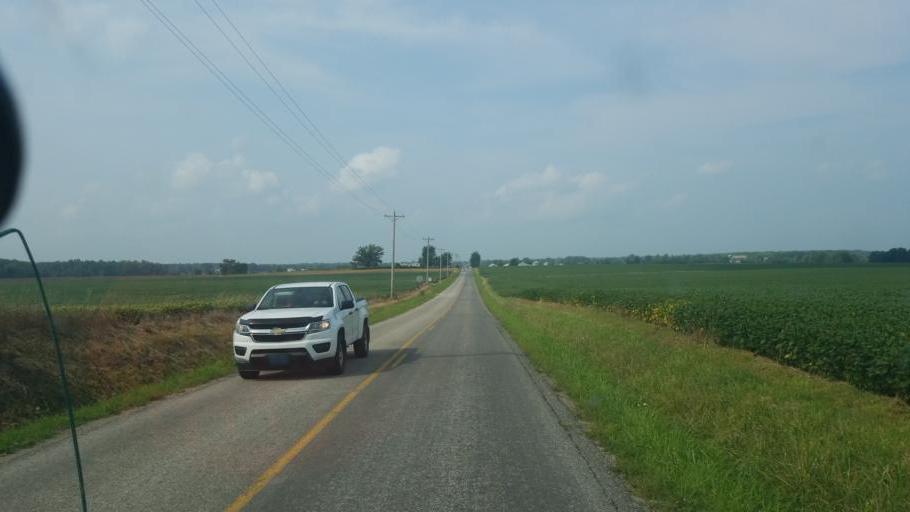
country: US
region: Ohio
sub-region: Lorain County
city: Wellington
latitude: 41.1028
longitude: -82.1611
